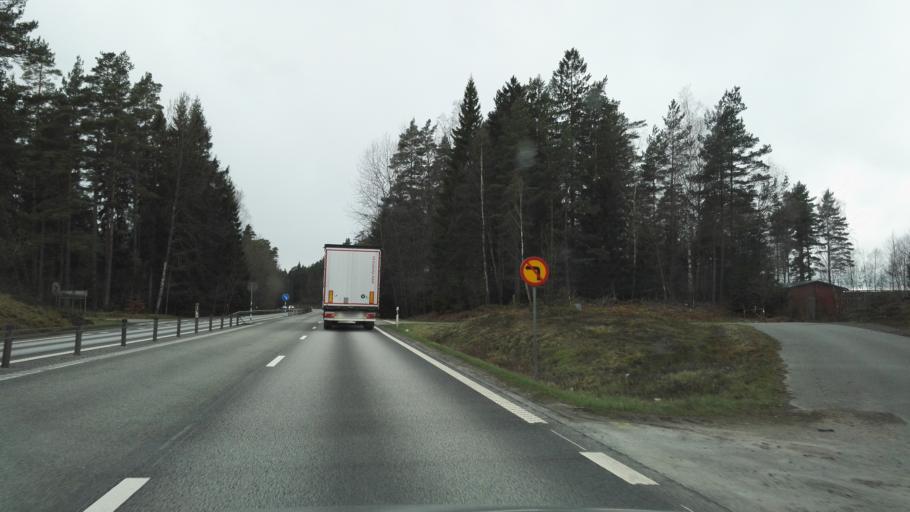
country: SE
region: Skane
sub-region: Osby Kommun
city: Osby
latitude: 56.3648
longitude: 14.0216
